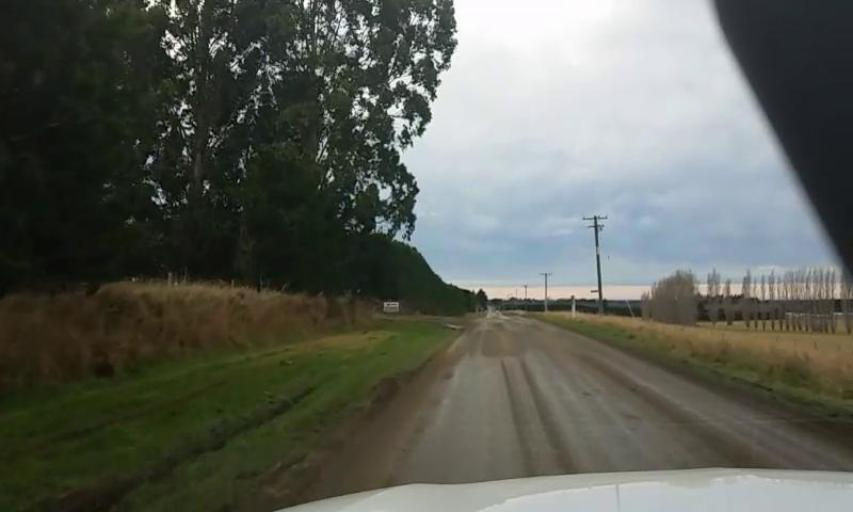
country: NZ
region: Canterbury
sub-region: Waimakariri District
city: Kaiapoi
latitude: -43.3000
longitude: 172.4863
